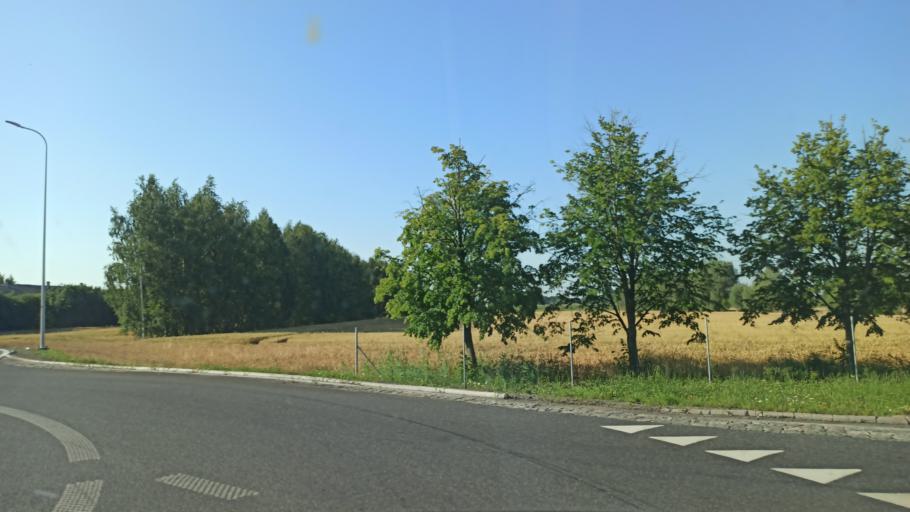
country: PL
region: Warmian-Masurian Voivodeship
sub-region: Powiat elblaski
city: Elblag
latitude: 54.1665
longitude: 19.3533
